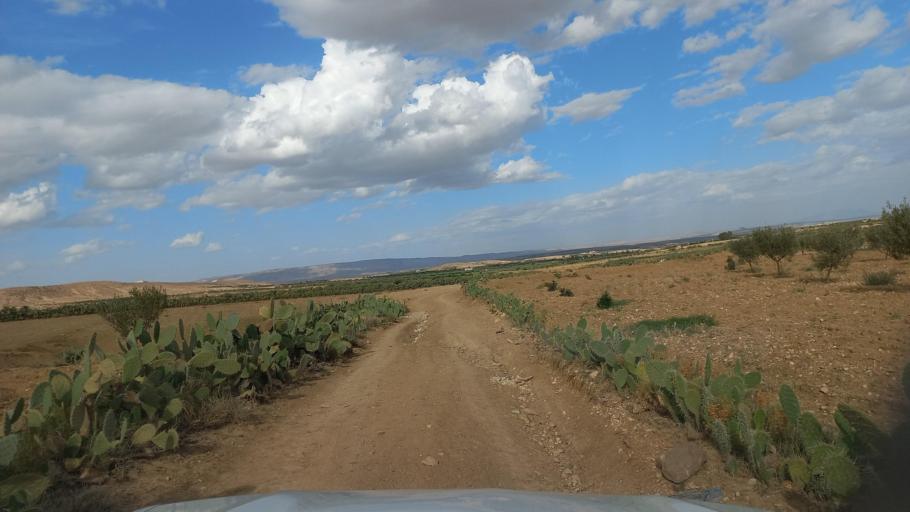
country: TN
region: Al Qasrayn
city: Sbiba
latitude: 35.4534
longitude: 9.0912
